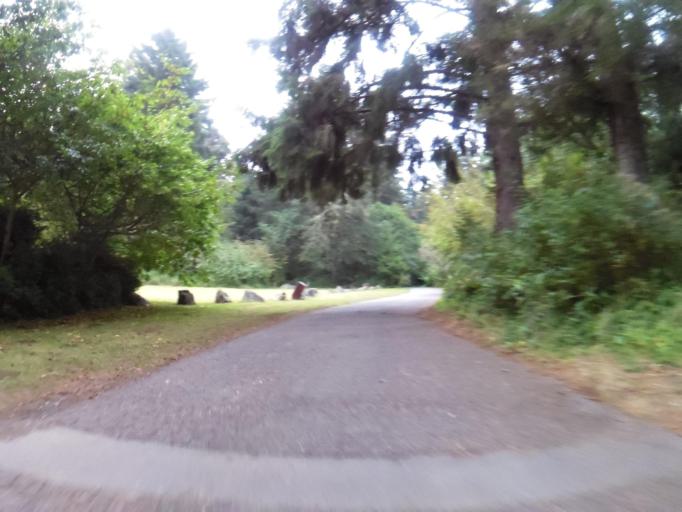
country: US
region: California
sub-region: Humboldt County
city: Westhaven-Moonstone
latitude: 41.1396
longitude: -124.1598
